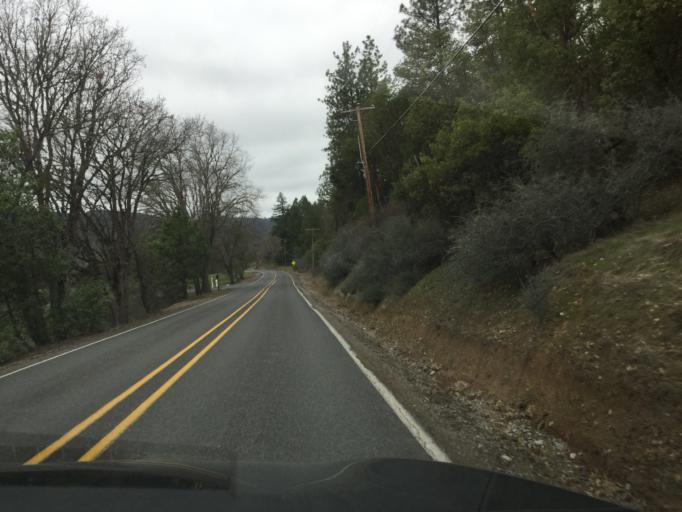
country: US
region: Oregon
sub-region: Jackson County
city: Gold Hill
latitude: 42.3973
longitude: -123.0109
